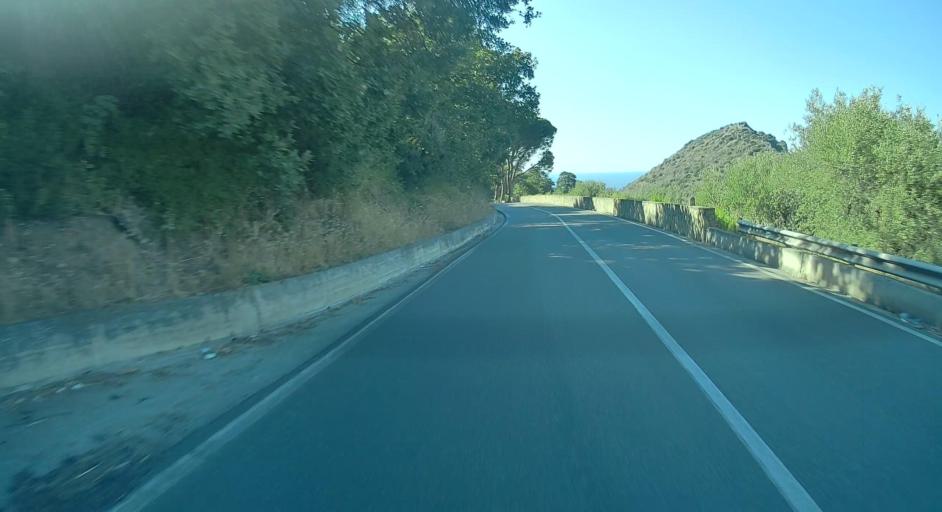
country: IT
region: Sicily
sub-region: Messina
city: Oliveri
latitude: 38.1401
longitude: 15.0299
